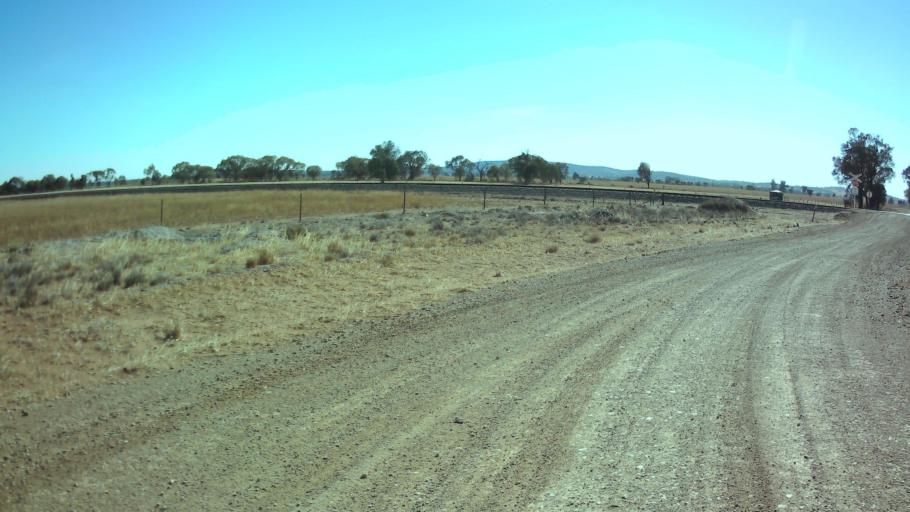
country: AU
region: New South Wales
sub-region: Weddin
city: Grenfell
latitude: -33.8313
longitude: 147.7427
